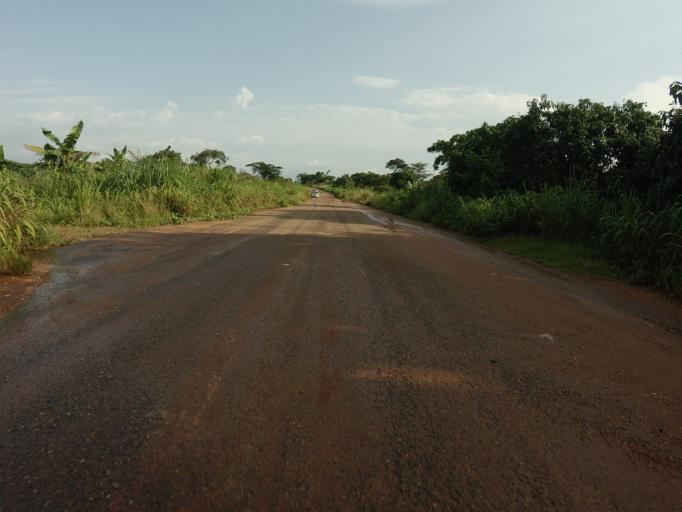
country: GH
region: Volta
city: Hohoe
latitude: 7.0930
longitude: 0.4457
